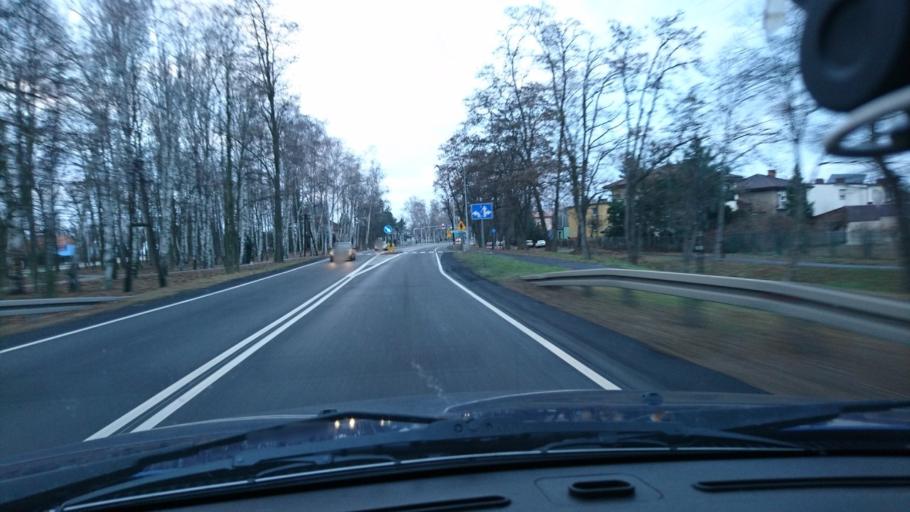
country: PL
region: Greater Poland Voivodeship
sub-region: Powiat ostrzeszowski
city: Ostrzeszow
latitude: 51.4199
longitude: 17.9280
